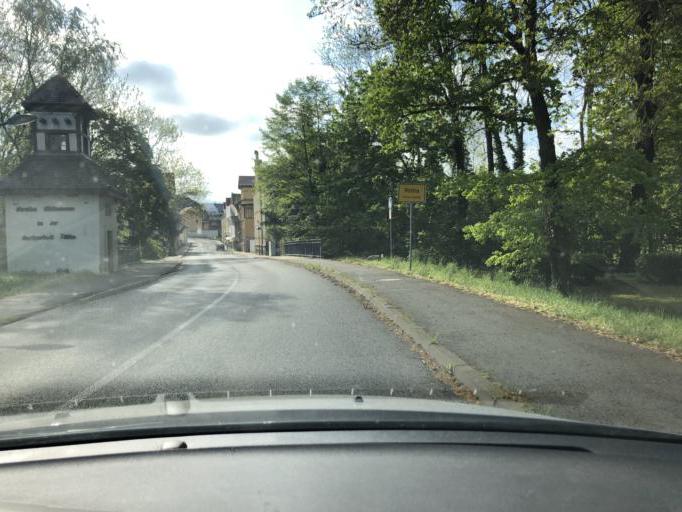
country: DE
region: Saxony
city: Rotha
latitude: 51.1991
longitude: 12.4067
